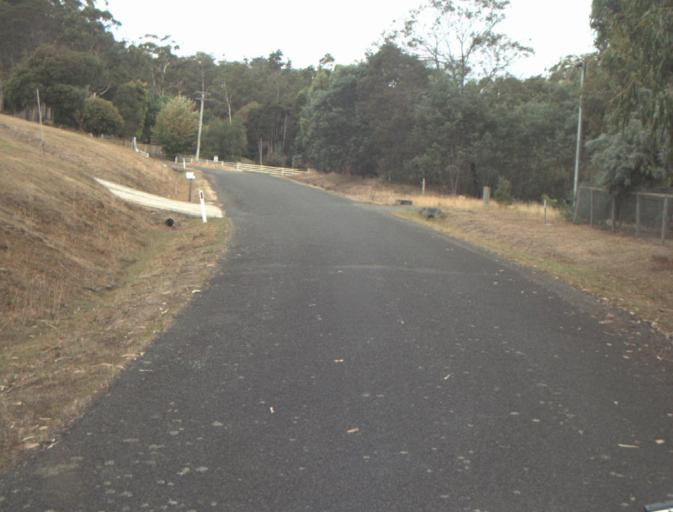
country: AU
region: Tasmania
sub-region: Launceston
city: Mayfield
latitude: -41.2794
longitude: 147.0213
